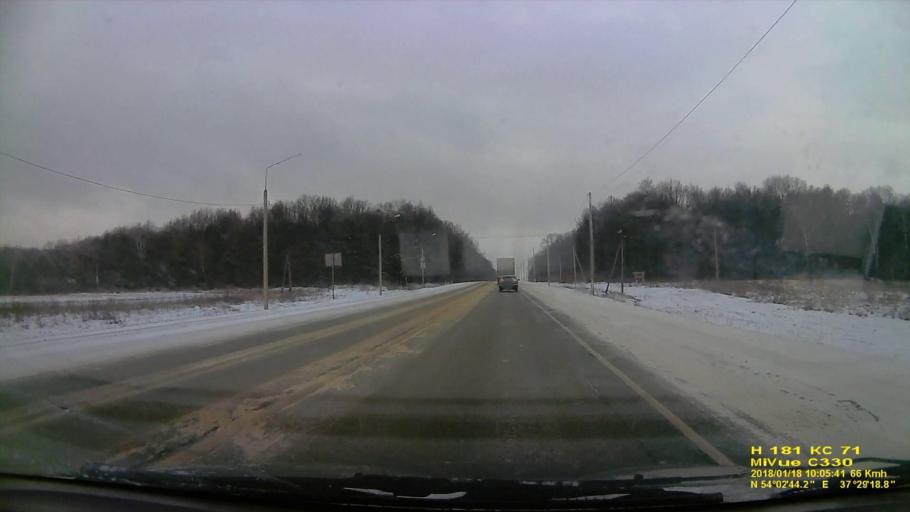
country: RU
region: Tula
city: Pervomayskiy
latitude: 54.0452
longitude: 37.4885
